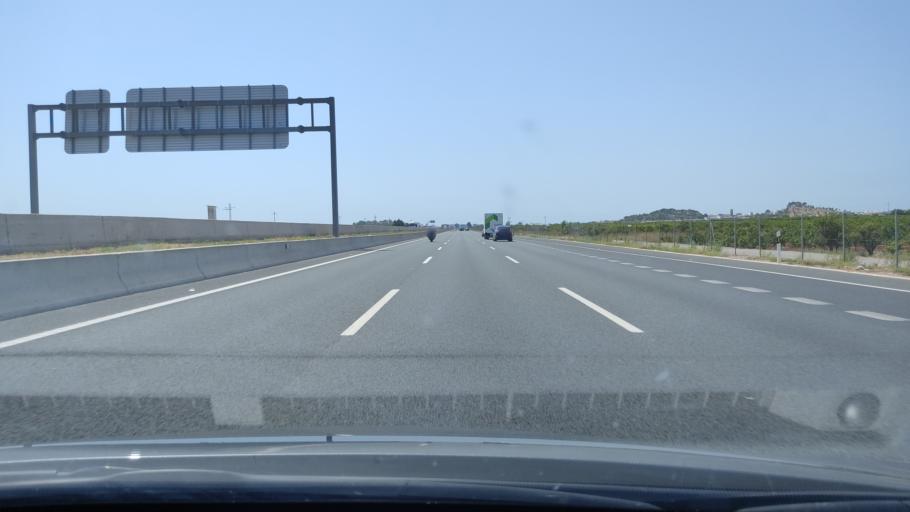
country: ES
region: Valencia
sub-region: Provincia de Valencia
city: Pucol
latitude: 39.6105
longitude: -0.2944
